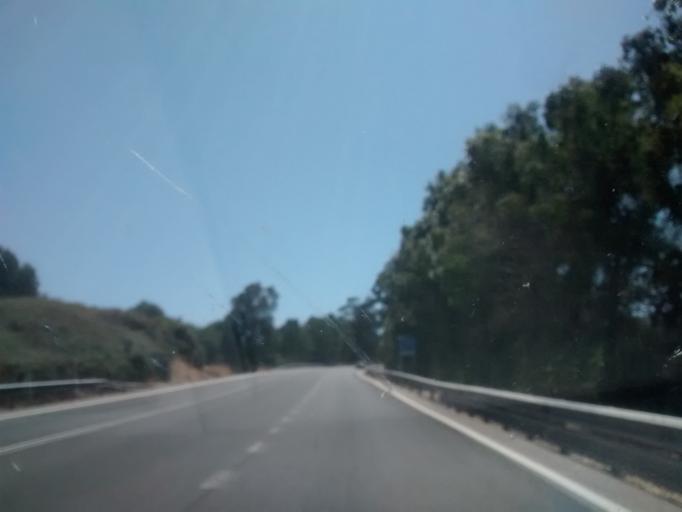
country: ES
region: Andalusia
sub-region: Provincia de Cadiz
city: Algeciras
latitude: 36.0954
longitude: -5.4722
